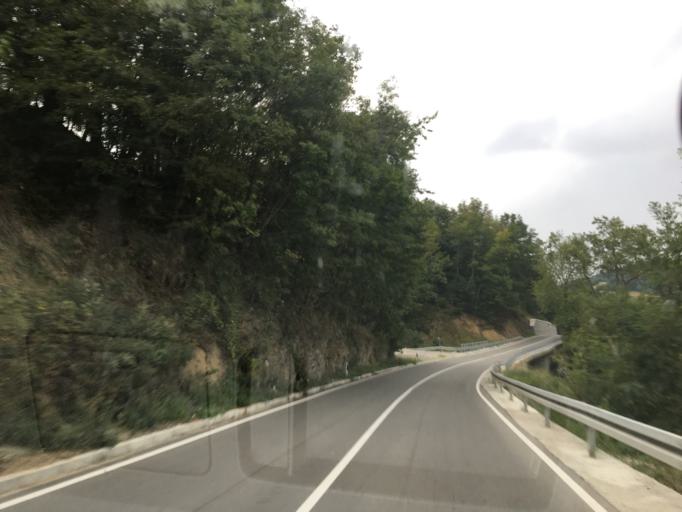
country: RS
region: Central Serbia
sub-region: Sumadijski Okrug
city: Arangelovac
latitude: 44.1729
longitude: 20.5224
